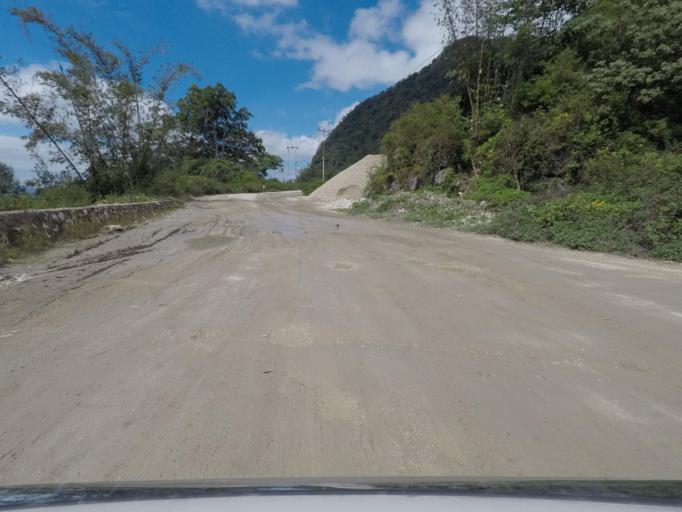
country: TL
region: Baucau
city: Venilale
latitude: -8.7111
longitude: 126.3641
